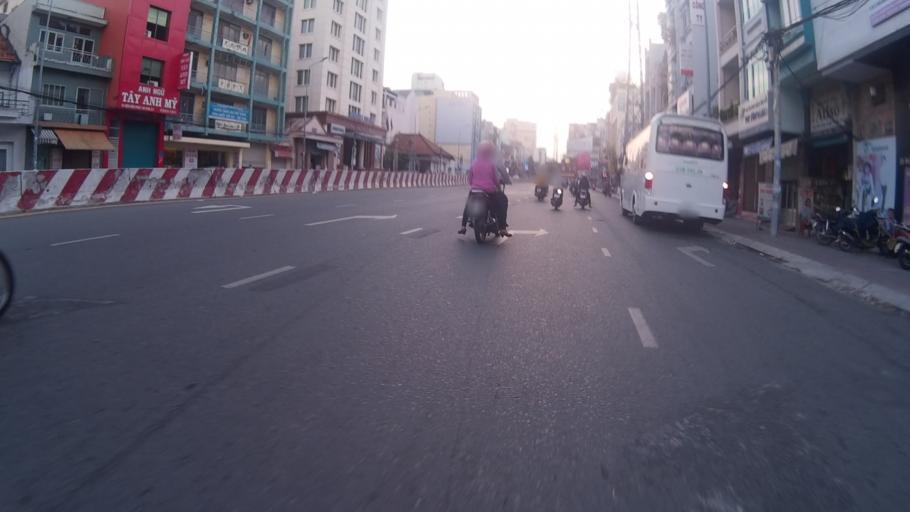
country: VN
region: Ho Chi Minh City
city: Quan Mot
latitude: 10.7919
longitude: 106.6989
